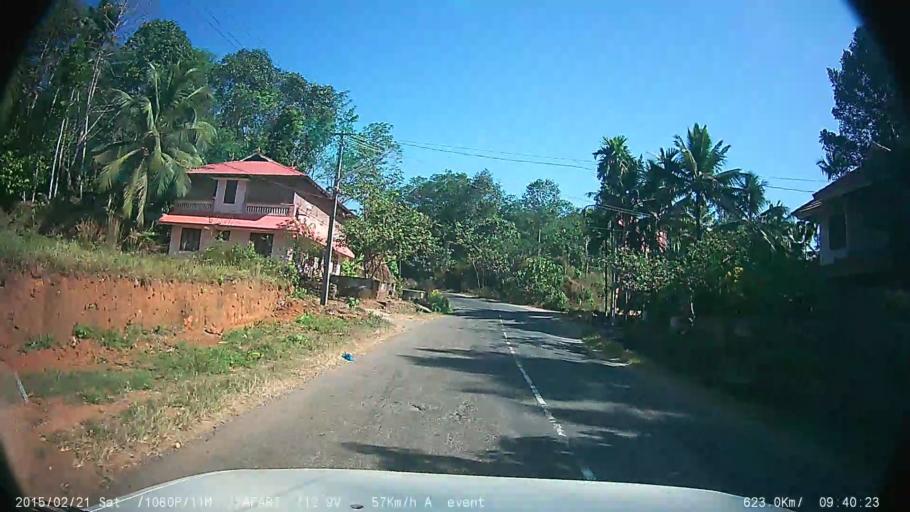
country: IN
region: Kerala
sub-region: Kottayam
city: Palackattumala
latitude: 9.7878
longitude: 76.5788
